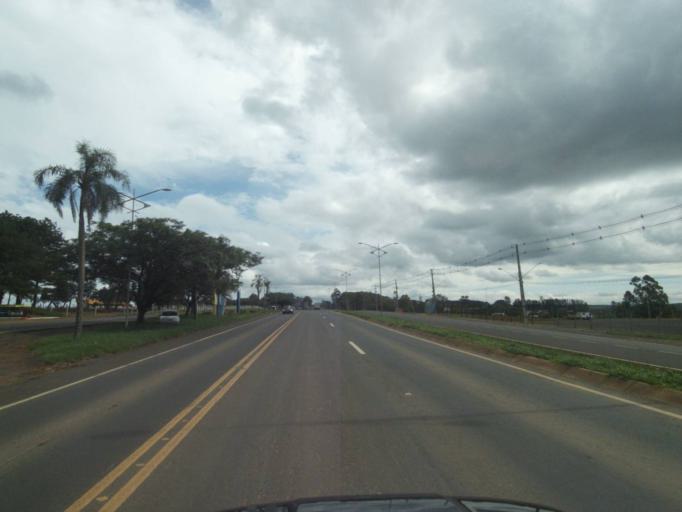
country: BR
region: Parana
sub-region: Telemaco Borba
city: Telemaco Borba
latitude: -24.3394
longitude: -50.6567
